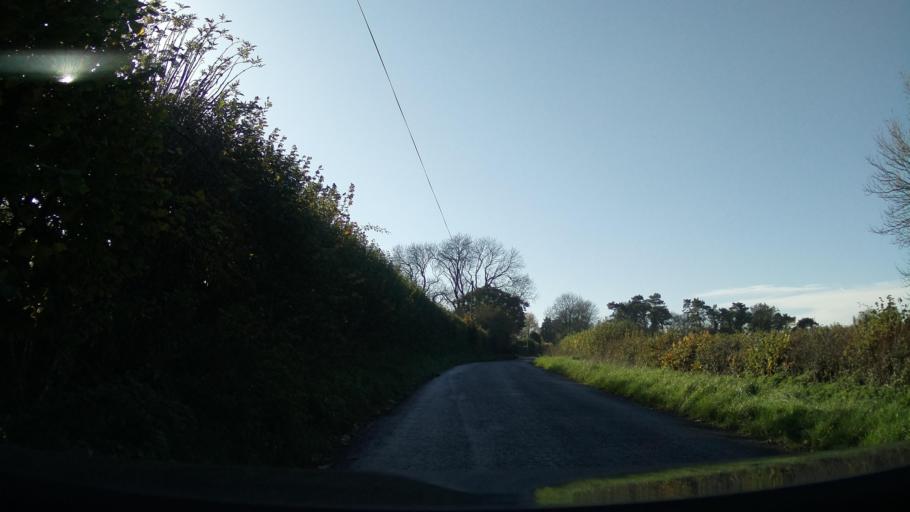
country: GB
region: England
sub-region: Somerset
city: Milborne Port
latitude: 51.0220
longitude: -2.4982
